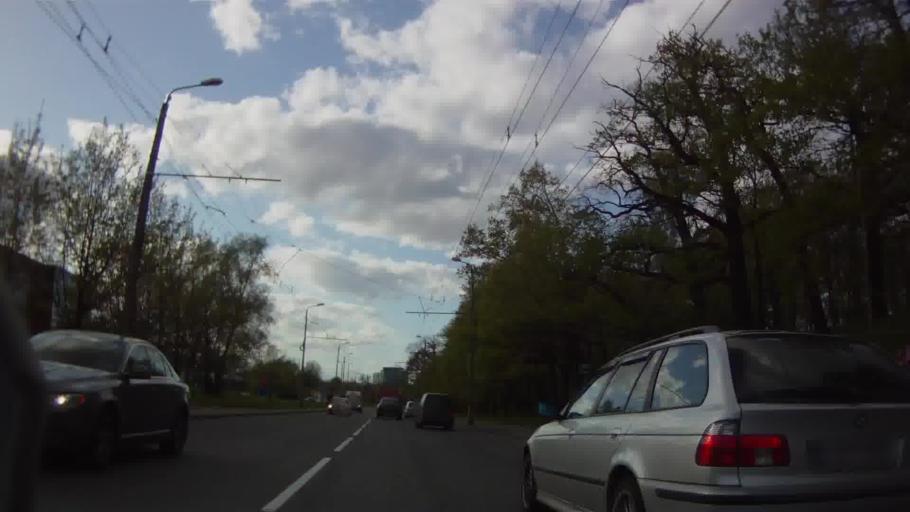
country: LV
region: Riga
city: Riga
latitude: 56.9872
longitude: 24.1328
